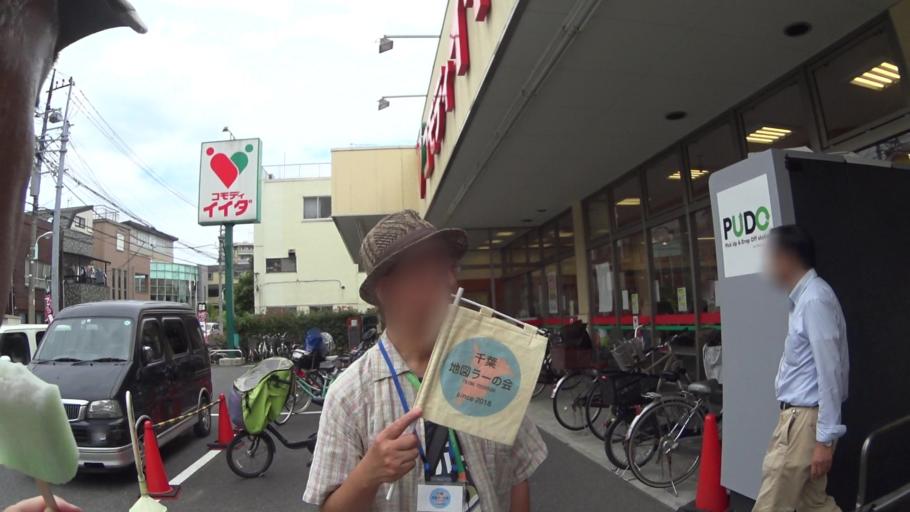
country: JP
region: Tokyo
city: Urayasu
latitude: 35.7119
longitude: 139.8386
